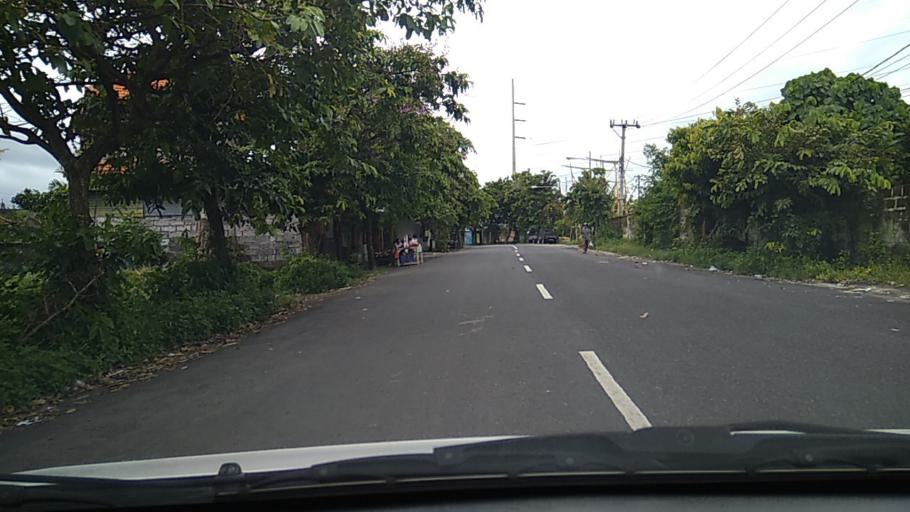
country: ID
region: Bali
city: Banjar Kertajiwa
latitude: -8.6573
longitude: 115.2592
